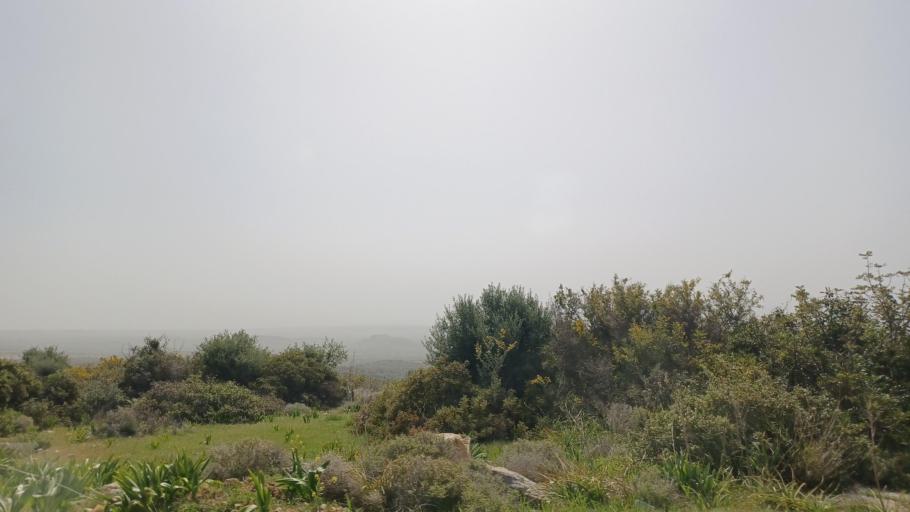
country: CY
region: Limassol
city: Pissouri
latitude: 34.7219
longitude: 32.7278
